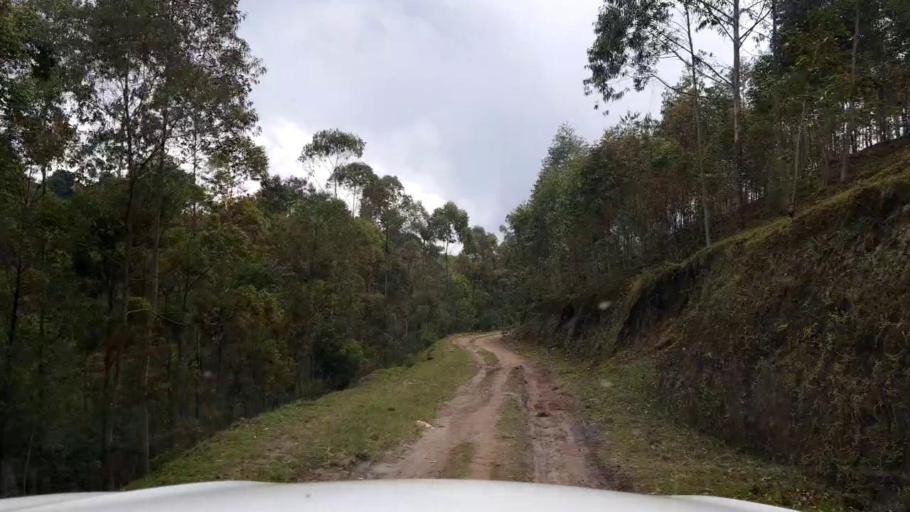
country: RW
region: Northern Province
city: Musanze
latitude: -1.5956
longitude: 29.7728
